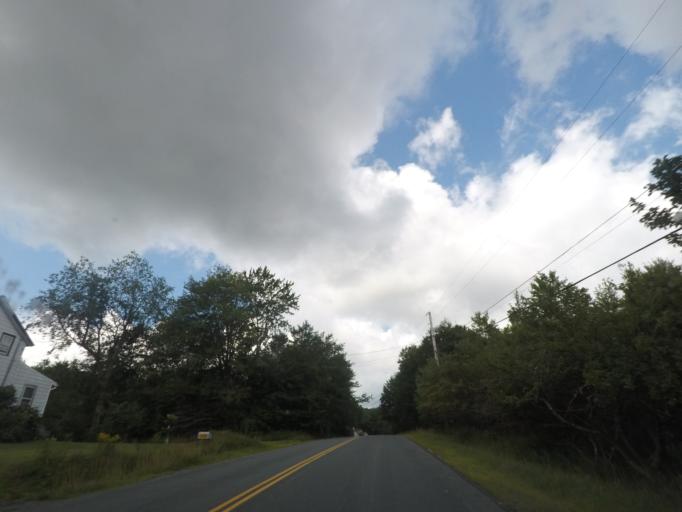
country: US
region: New York
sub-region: Rensselaer County
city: Averill Park
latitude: 42.6375
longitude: -73.4615
